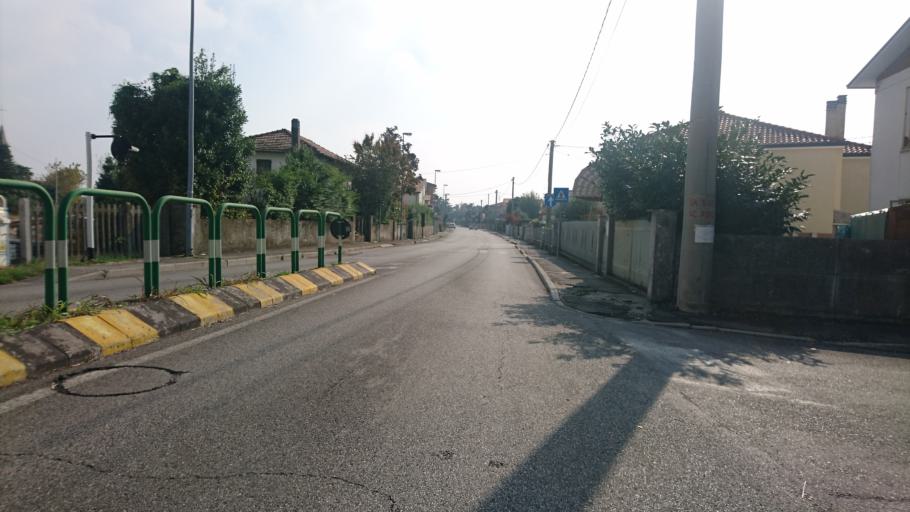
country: IT
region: Veneto
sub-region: Provincia di Rovigo
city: Rovigo
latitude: 45.0629
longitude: 11.7836
